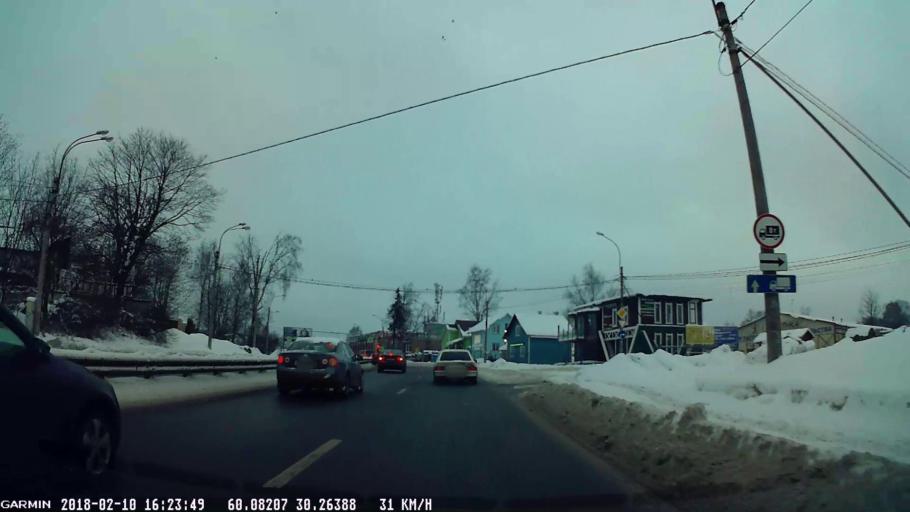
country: RU
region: St.-Petersburg
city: Pargolovo
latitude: 60.0823
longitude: 30.2634
